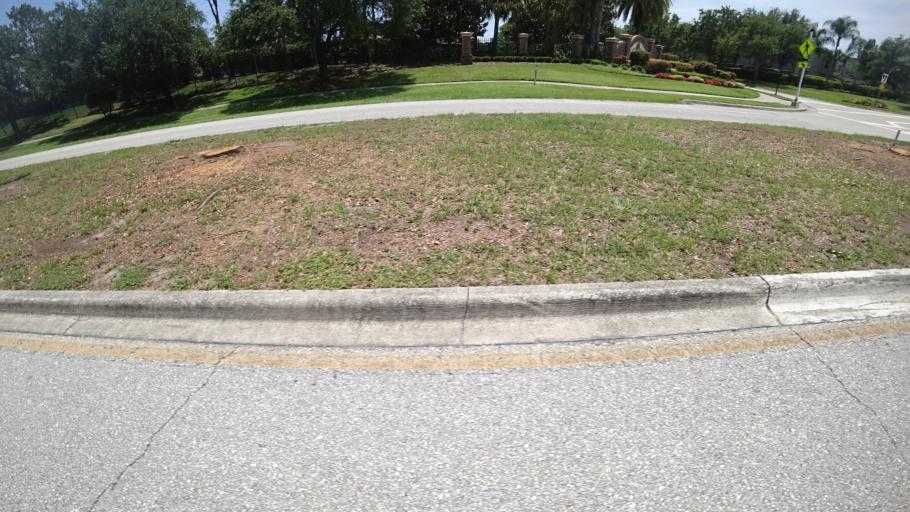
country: US
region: Florida
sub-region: Sarasota County
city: The Meadows
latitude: 27.3996
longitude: -82.4632
